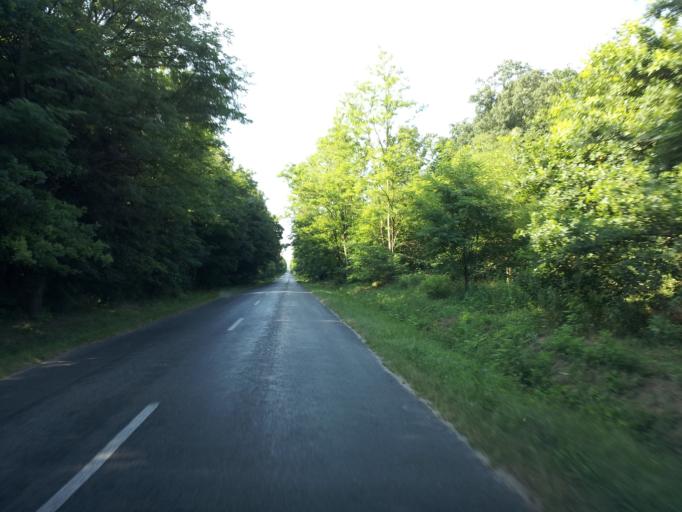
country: HU
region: Zala
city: Cserszegtomaj
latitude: 46.8500
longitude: 17.1979
